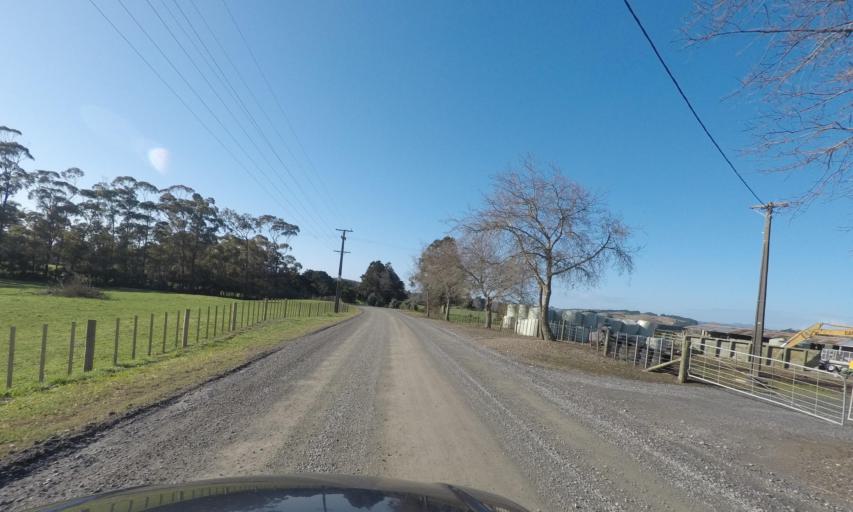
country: NZ
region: Auckland
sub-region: Auckland
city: Wellsford
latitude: -36.1462
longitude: 174.6009
